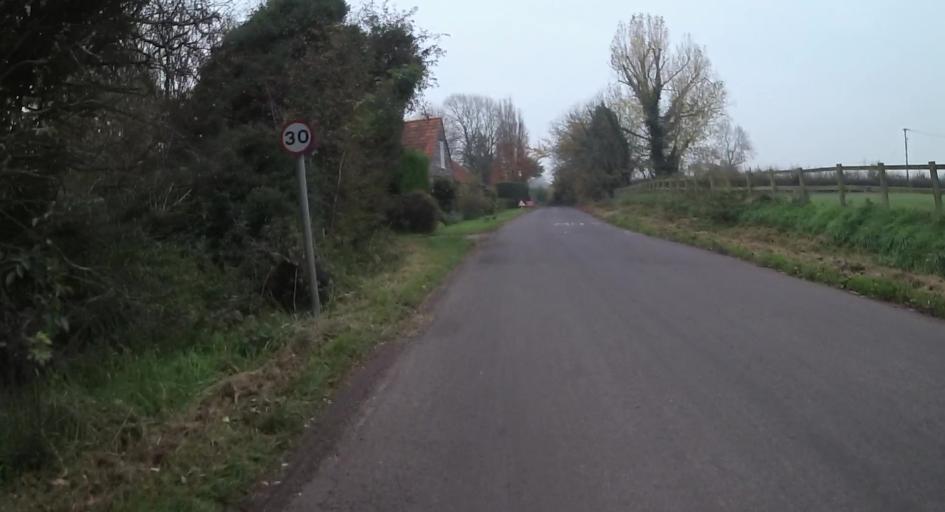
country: GB
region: England
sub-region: Hampshire
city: Long Sutton
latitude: 51.1902
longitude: -0.9056
